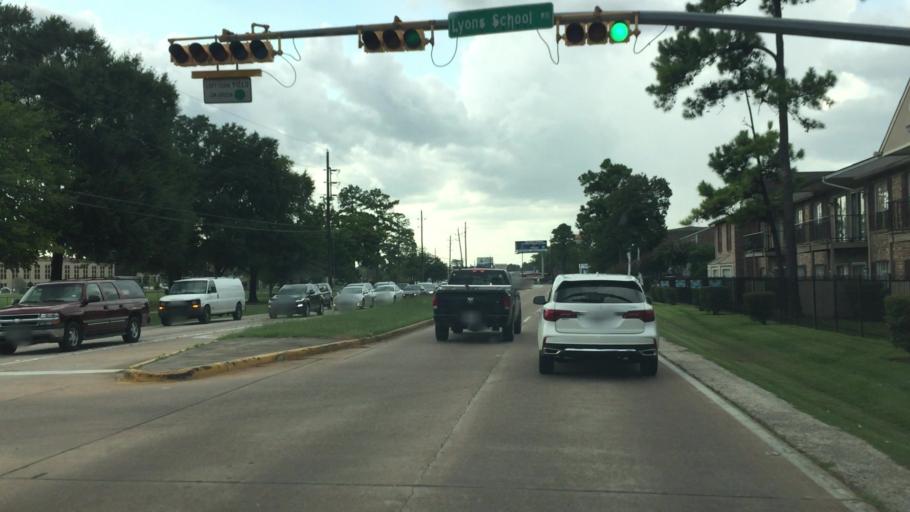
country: US
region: Texas
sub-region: Harris County
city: Hudson
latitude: 30.0167
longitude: -95.5192
